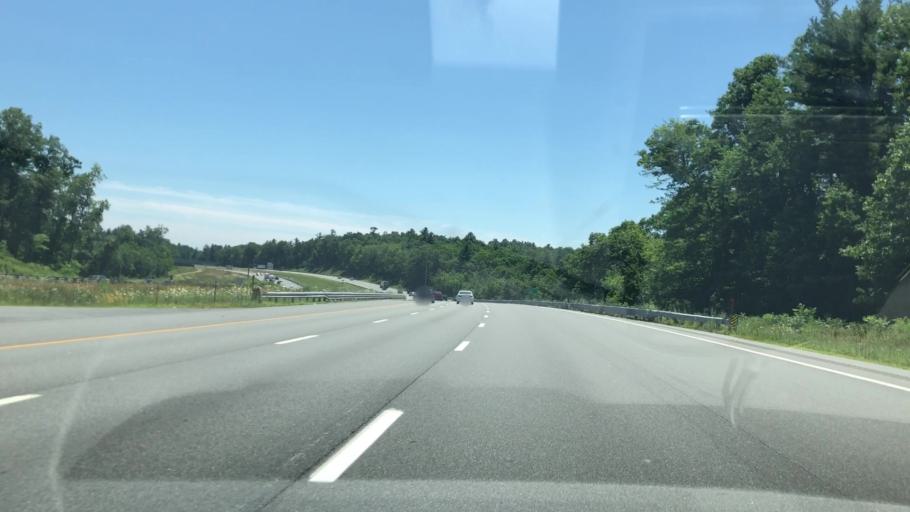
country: US
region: New Hampshire
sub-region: Rockingham County
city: Windham
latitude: 42.7932
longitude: -71.2720
